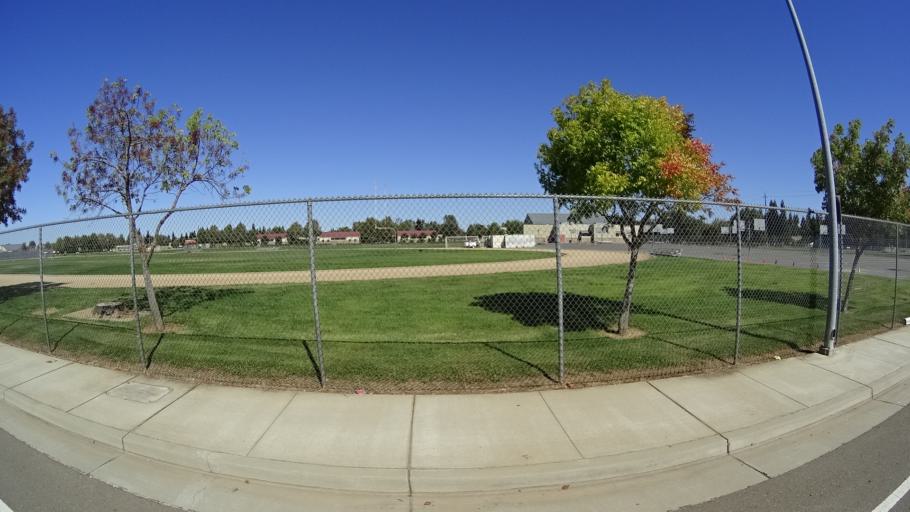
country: US
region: California
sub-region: Sacramento County
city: Elk Grove
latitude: 38.4237
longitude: -121.3358
